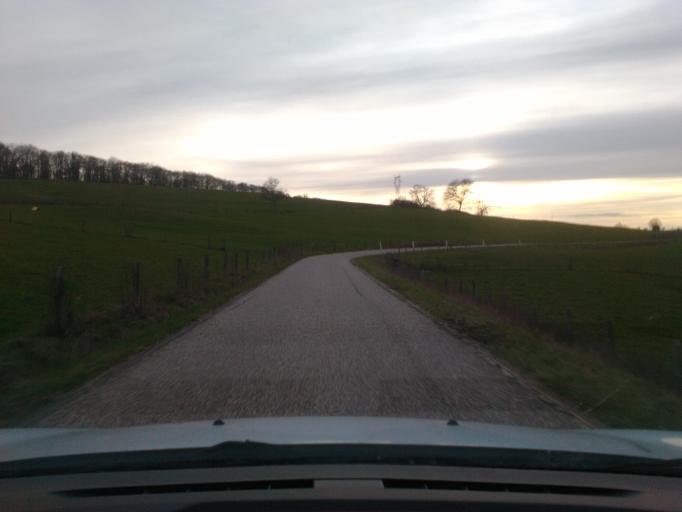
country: FR
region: Lorraine
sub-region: Departement des Vosges
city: Portieux
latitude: 48.3492
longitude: 6.3755
